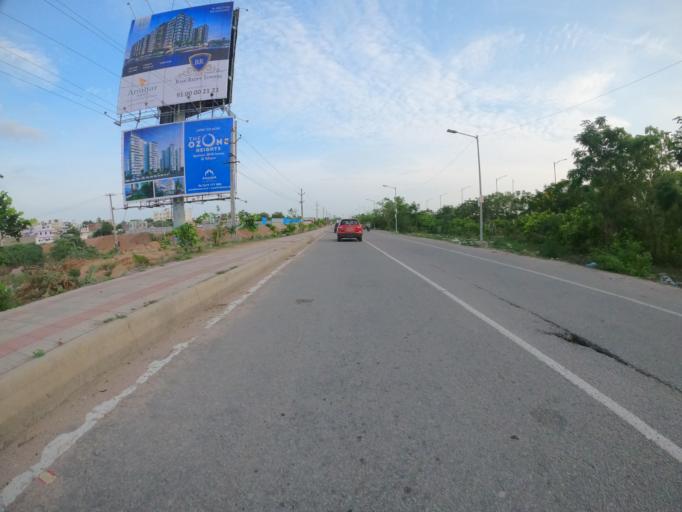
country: IN
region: Telangana
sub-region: Hyderabad
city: Hyderabad
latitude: 17.3916
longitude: 78.3525
